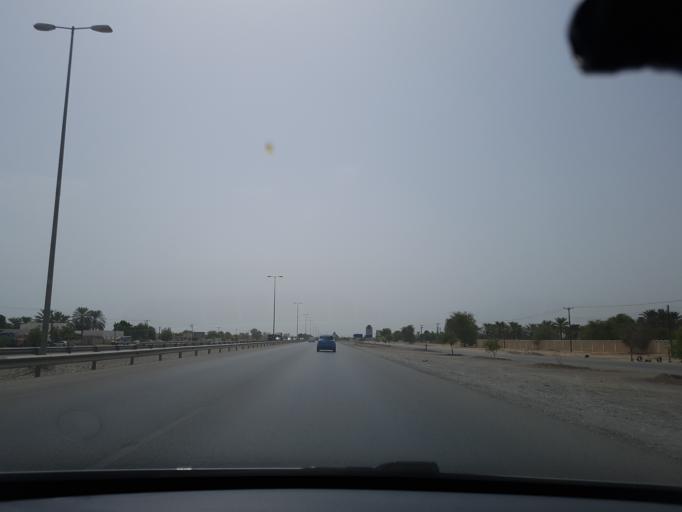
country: OM
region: Al Batinah
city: As Suwayq
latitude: 23.8130
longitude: 57.4568
